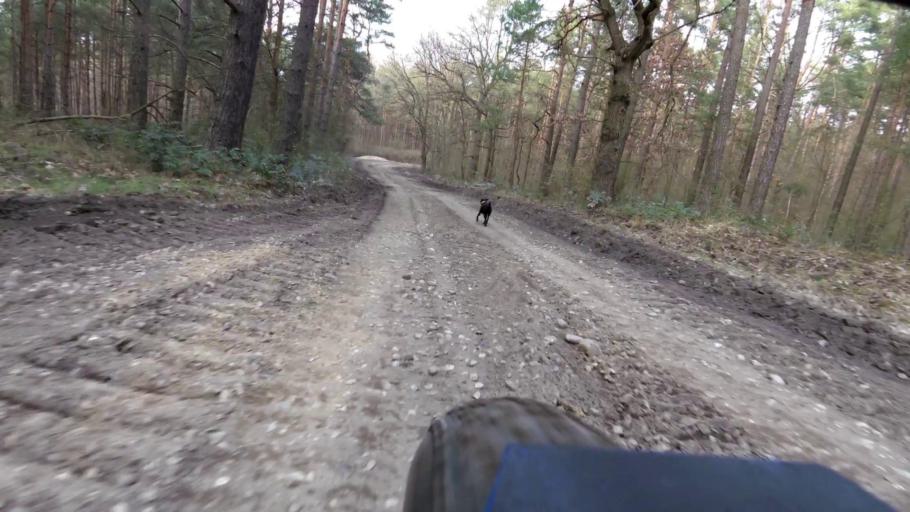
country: DE
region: Brandenburg
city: Vogelsang
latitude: 52.2768
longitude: 14.6956
